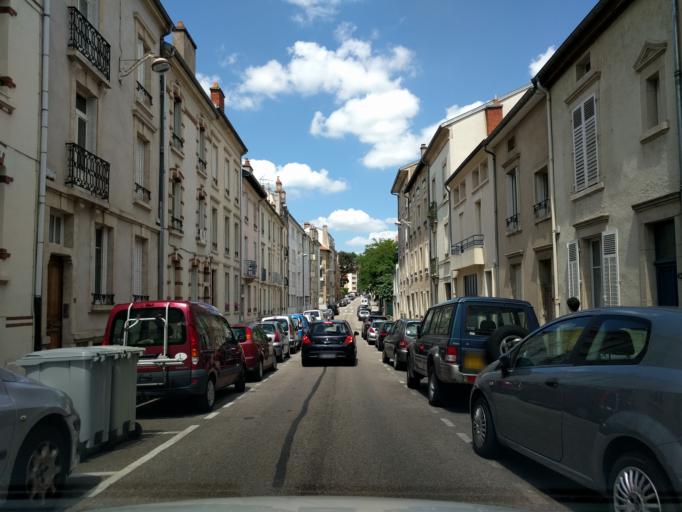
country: FR
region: Lorraine
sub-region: Departement de Meurthe-et-Moselle
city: Laxou
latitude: 48.6840
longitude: 6.1649
